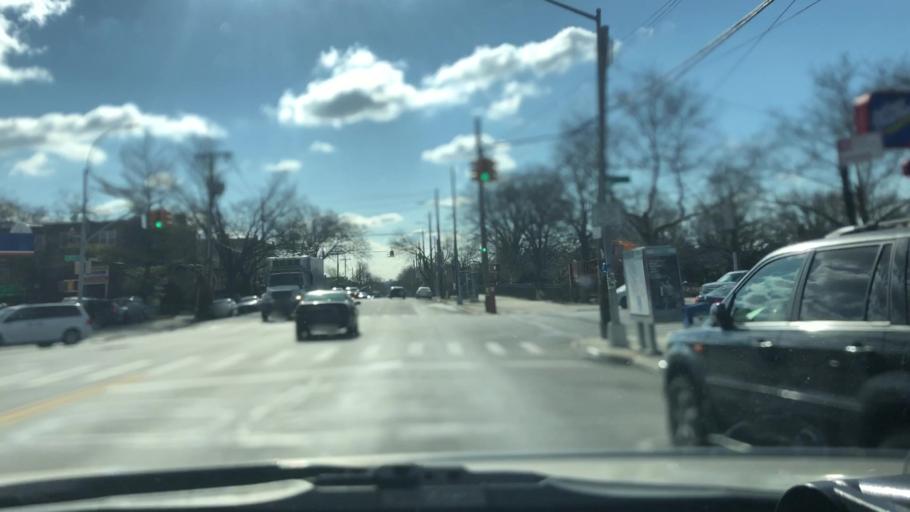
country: US
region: New York
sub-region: Kings County
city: Bensonhurst
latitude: 40.6187
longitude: -74.0216
